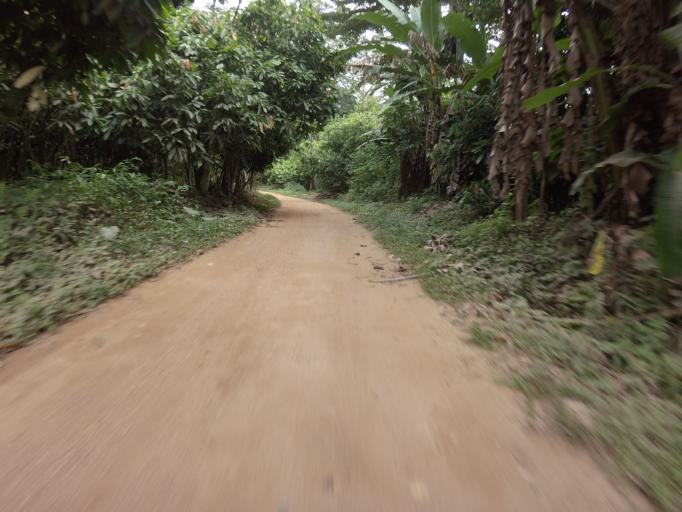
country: GH
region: Volta
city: Kpandu
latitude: 6.8828
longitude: 0.4371
